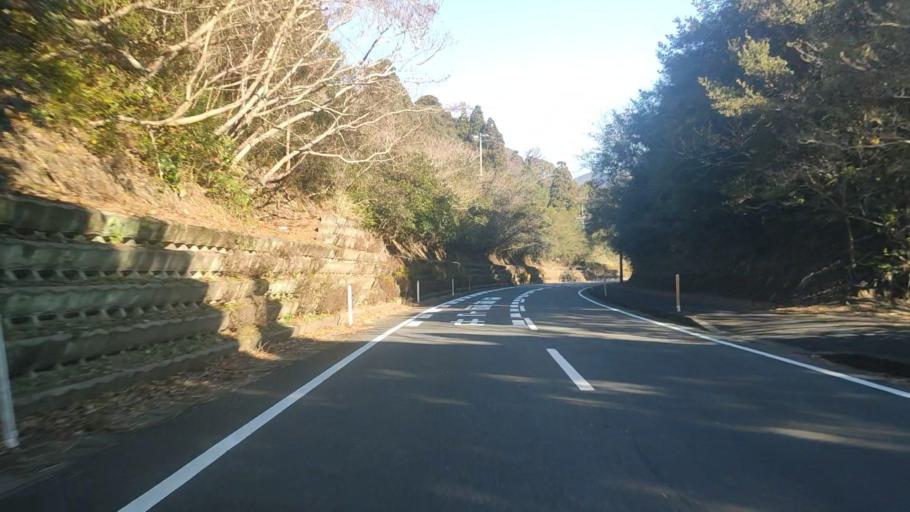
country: JP
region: Miyazaki
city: Nobeoka
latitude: 32.7040
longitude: 131.8158
